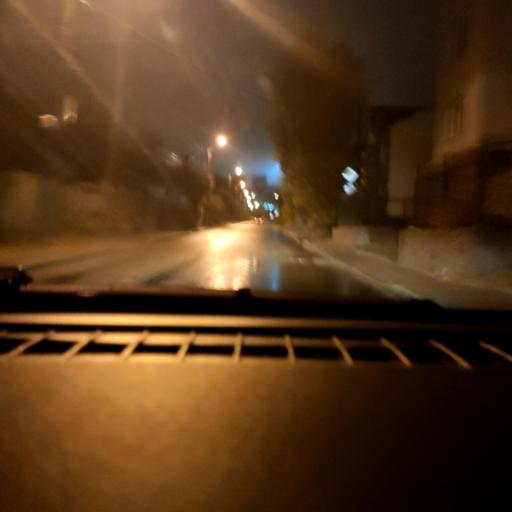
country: RU
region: Voronezj
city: Voronezh
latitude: 51.6521
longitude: 39.2063
